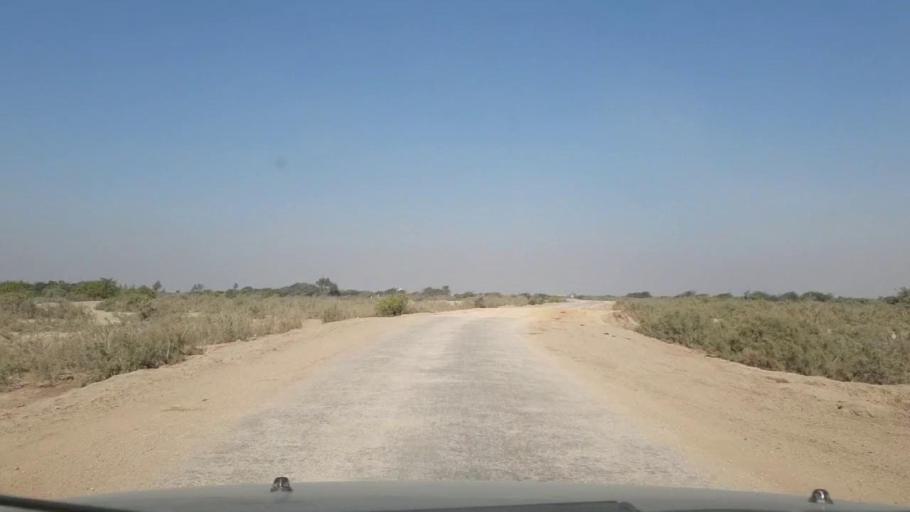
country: PK
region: Sindh
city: Thatta
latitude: 24.8063
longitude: 67.9011
